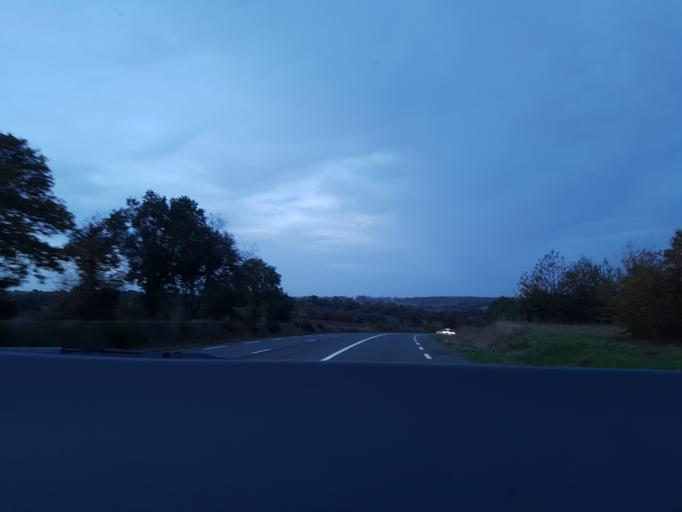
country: FR
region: Pays de la Loire
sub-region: Departement de la Mayenne
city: Montigne-le-Brillant
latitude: 48.0196
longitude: -0.8237
